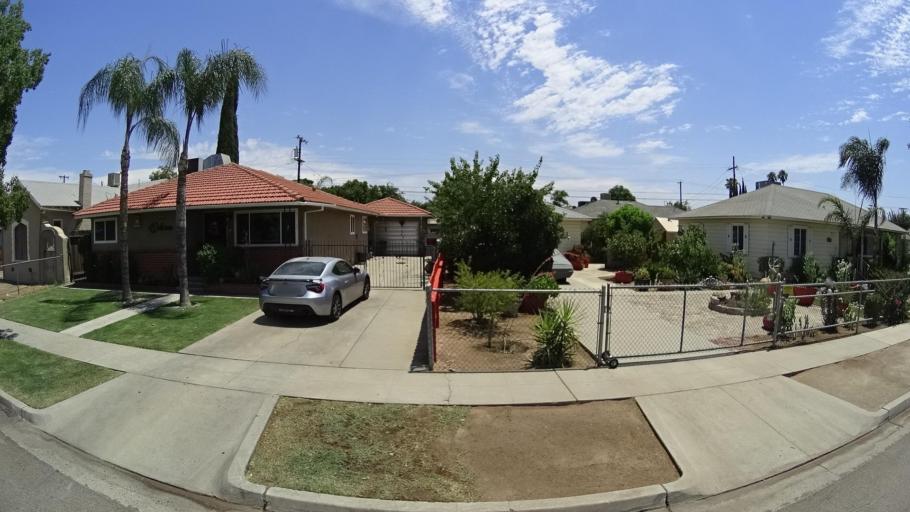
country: US
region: California
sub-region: Fresno County
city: Fresno
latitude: 36.7264
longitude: -119.7670
